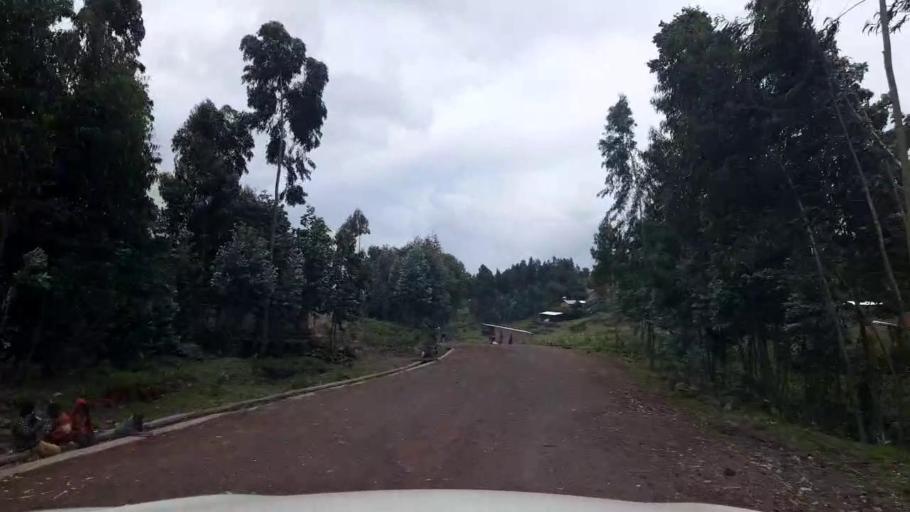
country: RW
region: Northern Province
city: Musanze
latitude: -1.5914
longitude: 29.4629
